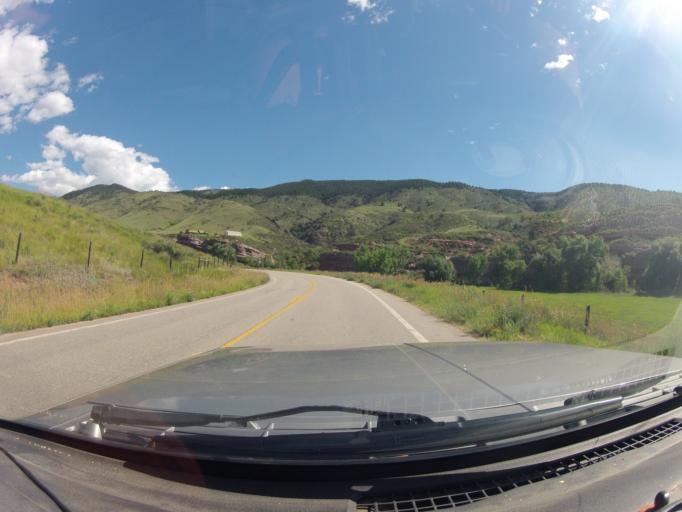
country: US
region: Colorado
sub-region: Larimer County
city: Laporte
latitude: 40.5177
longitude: -105.2506
